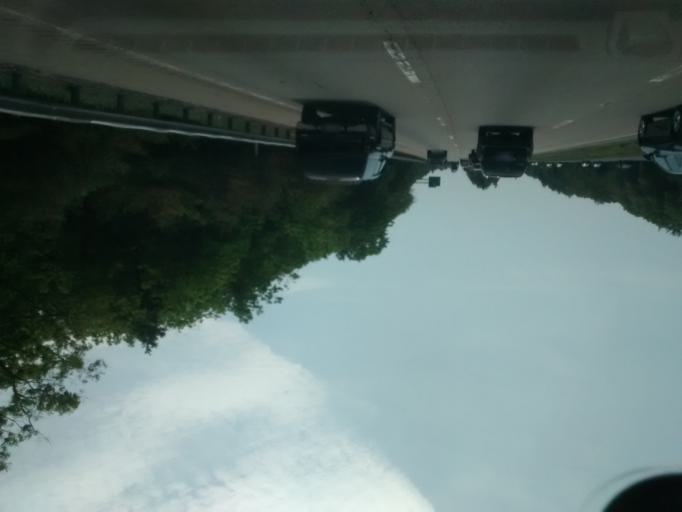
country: US
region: Massachusetts
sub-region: Norfolk County
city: Wrentham
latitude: 42.0499
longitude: -71.3661
